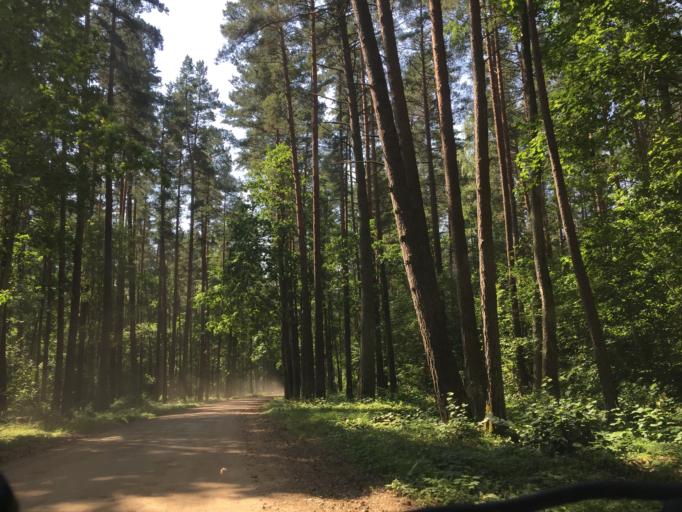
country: LV
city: Tervete
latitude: 56.4872
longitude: 23.4011
